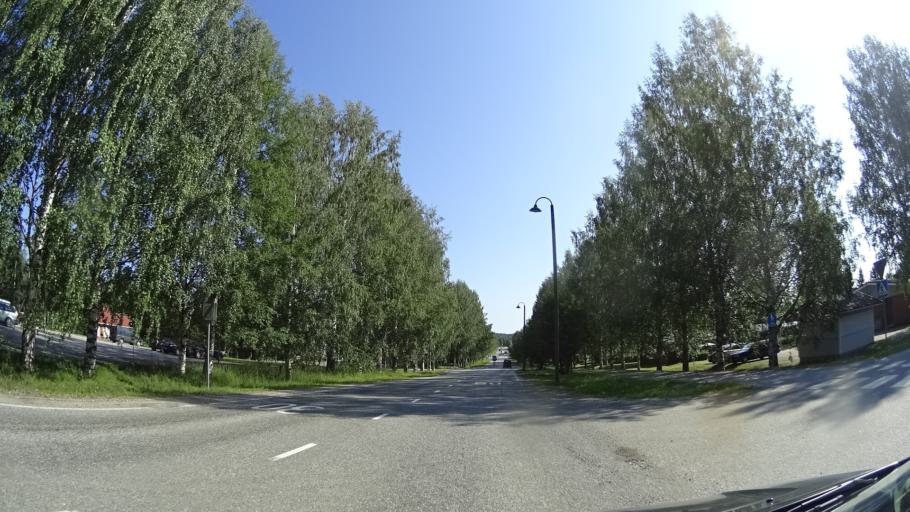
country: FI
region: North Karelia
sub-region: Joensuu
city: Juuka
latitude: 63.2439
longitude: 29.2561
